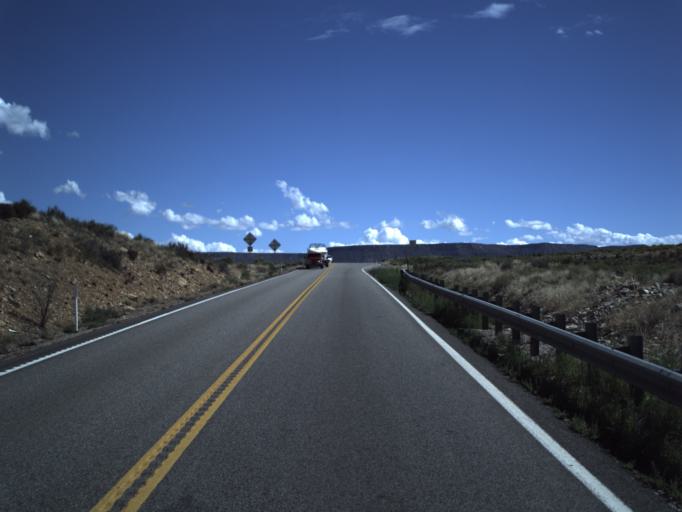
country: US
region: Utah
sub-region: Washington County
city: Hurricane
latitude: 37.1665
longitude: -113.2636
